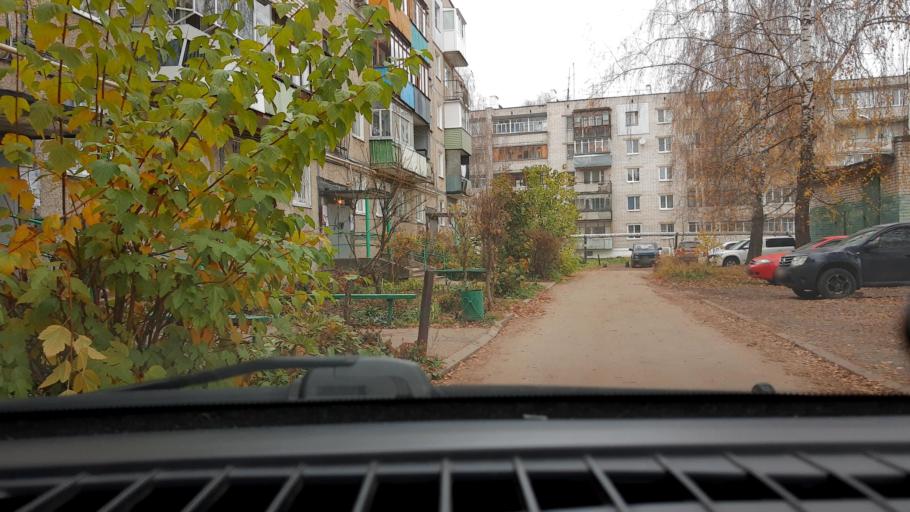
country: RU
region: Nizjnij Novgorod
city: Kstovo
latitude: 56.1818
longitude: 44.1639
